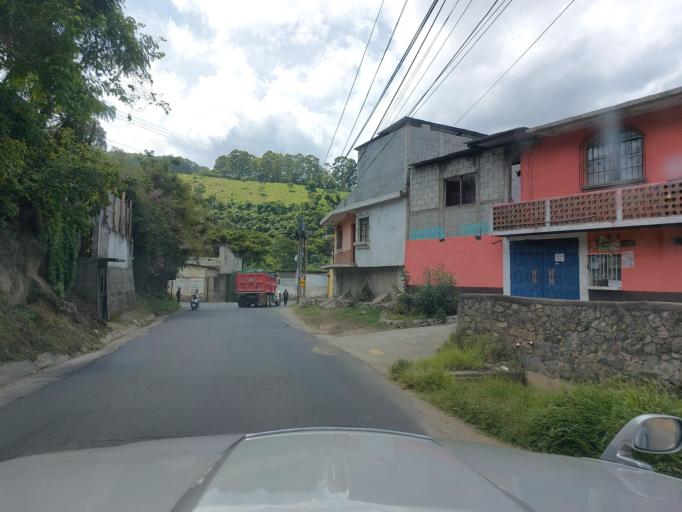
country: GT
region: Sacatepequez
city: Pastores
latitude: 14.6051
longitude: -90.7644
